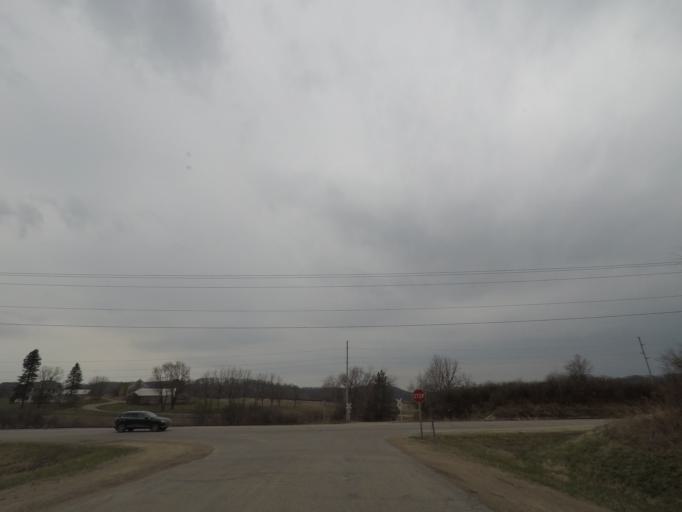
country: US
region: Wisconsin
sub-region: Dane County
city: Cross Plains
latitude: 43.0957
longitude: -89.6115
